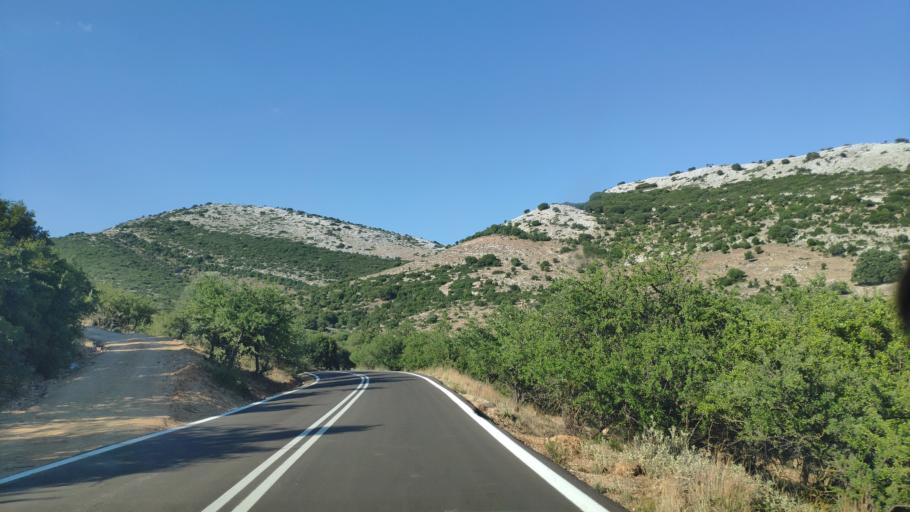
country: GR
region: West Greece
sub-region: Nomos Aitolias kai Akarnanias
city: Archontochorion
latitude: 38.6925
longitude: 21.0574
